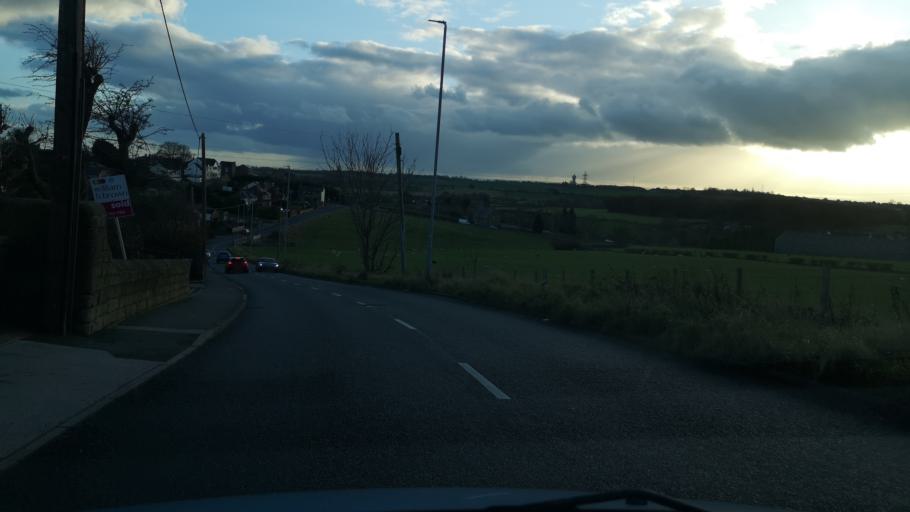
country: GB
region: England
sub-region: City and Borough of Leeds
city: Morley
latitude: 53.7194
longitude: -1.5817
